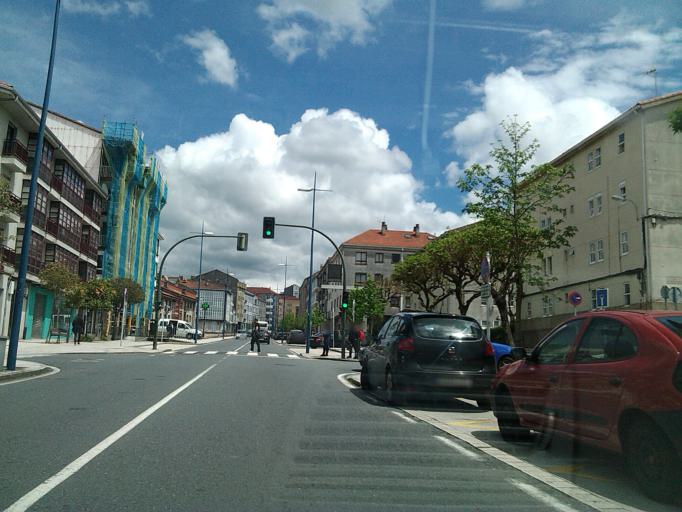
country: ES
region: Galicia
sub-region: Provincia da Coruna
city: Santiago de Compostela
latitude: 42.8704
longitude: -8.5582
